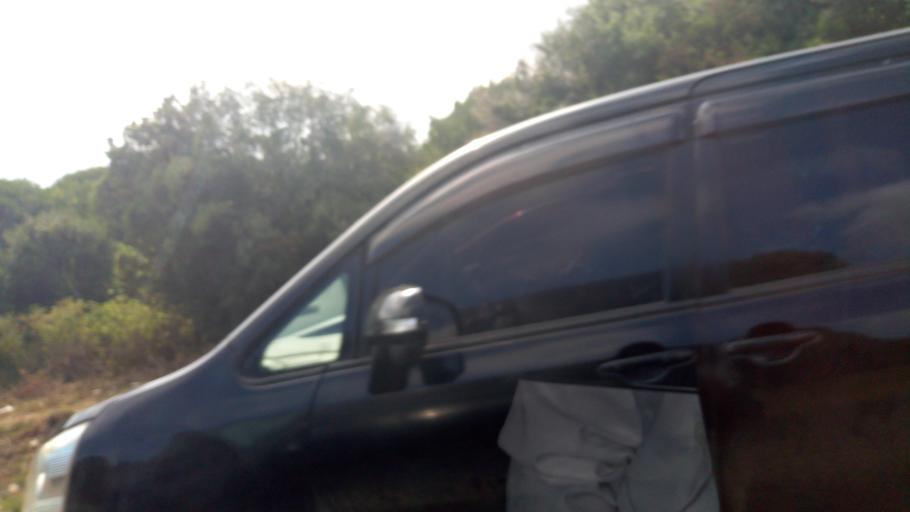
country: KE
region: Kiambu
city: Limuru
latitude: -1.0808
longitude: 36.6031
